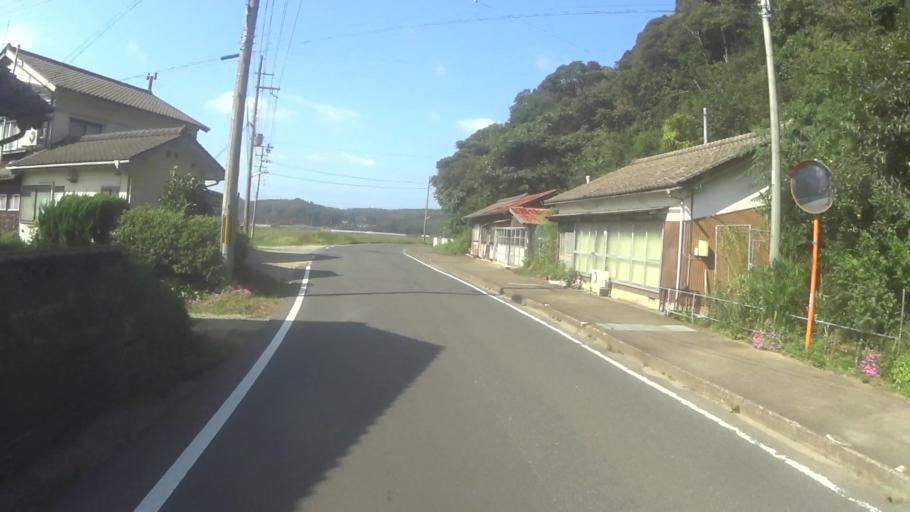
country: JP
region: Kyoto
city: Miyazu
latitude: 35.6860
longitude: 135.0517
